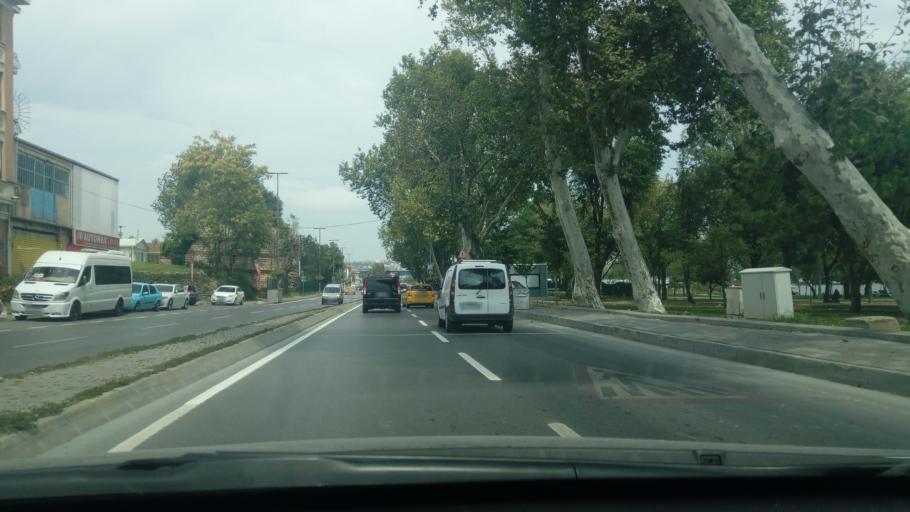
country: TR
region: Istanbul
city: Istanbul
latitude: 41.0355
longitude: 28.9461
